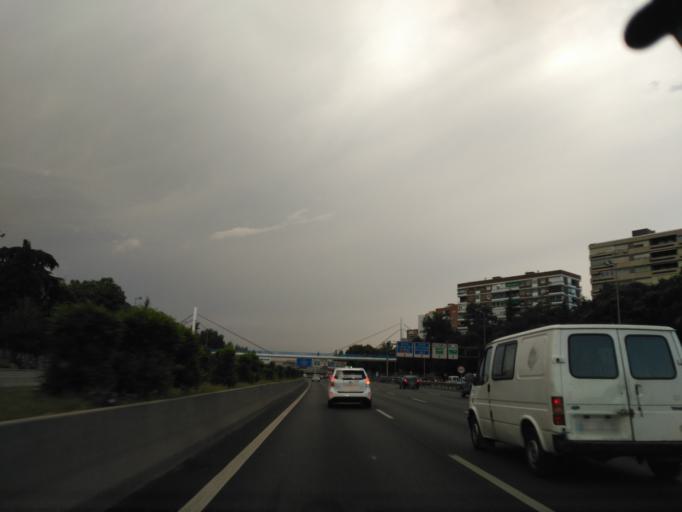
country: ES
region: Madrid
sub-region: Provincia de Madrid
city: Moratalaz
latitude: 40.4232
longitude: -3.6593
